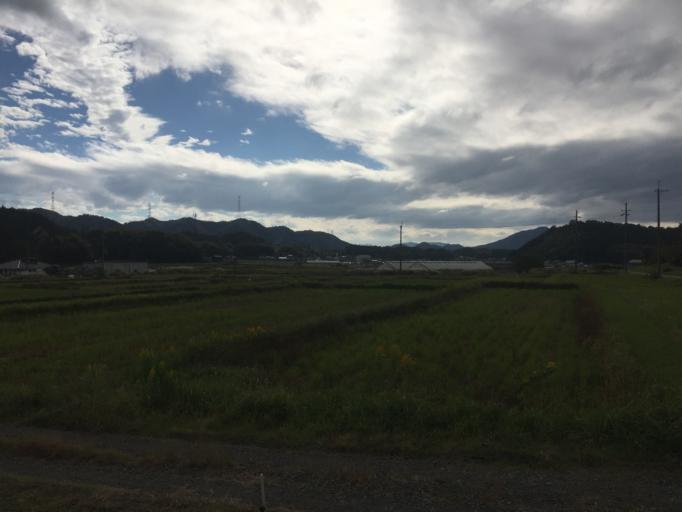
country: JP
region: Kyoto
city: Ayabe
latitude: 35.3626
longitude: 135.2444
